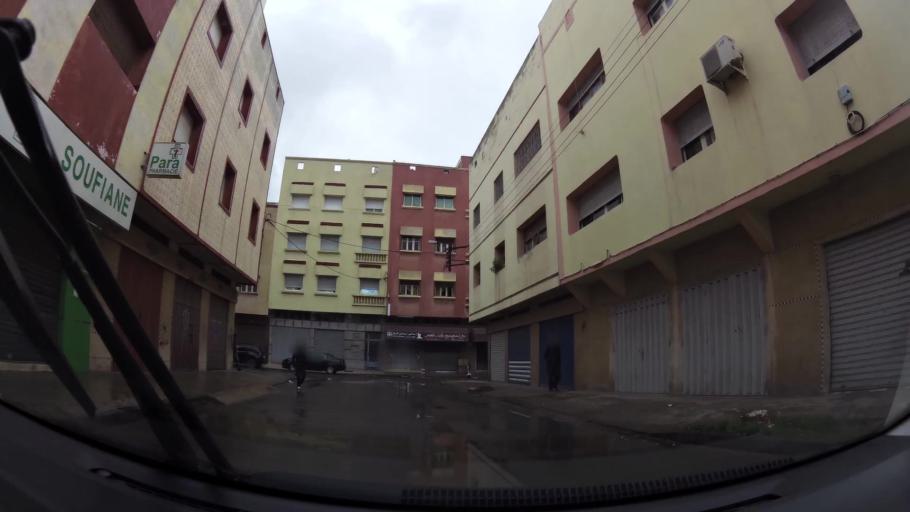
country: MA
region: Grand Casablanca
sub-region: Casablanca
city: Casablanca
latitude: 33.5493
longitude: -7.6814
